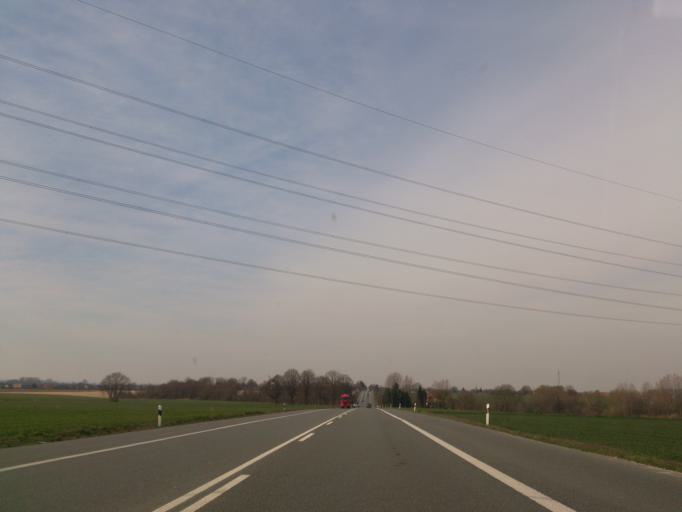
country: DE
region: North Rhine-Westphalia
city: Erwitte
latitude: 51.6002
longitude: 8.2709
